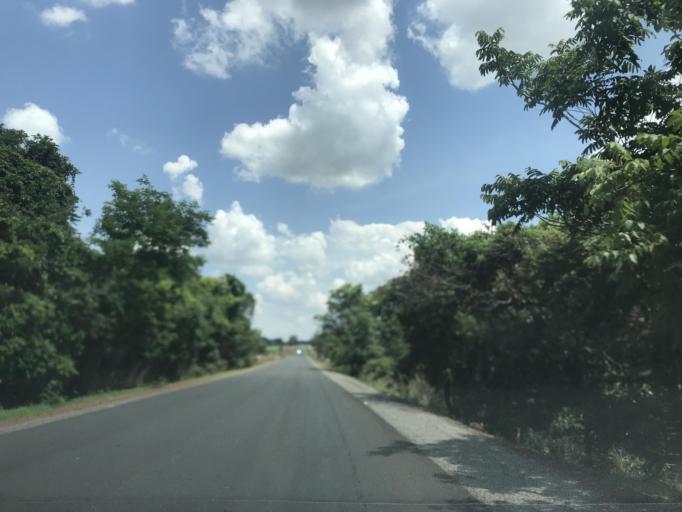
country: BR
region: Goias
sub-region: Piracanjuba
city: Piracanjuba
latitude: -17.3300
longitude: -48.8003
